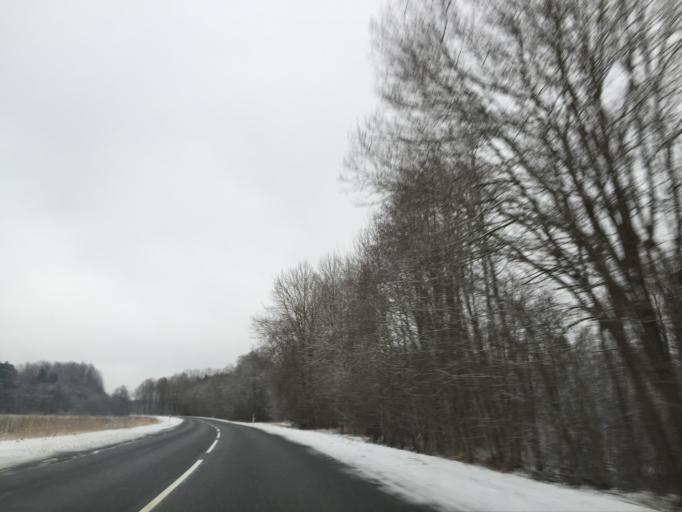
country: EE
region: Laeaene
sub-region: Lihula vald
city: Lihula
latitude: 58.6531
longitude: 23.8379
